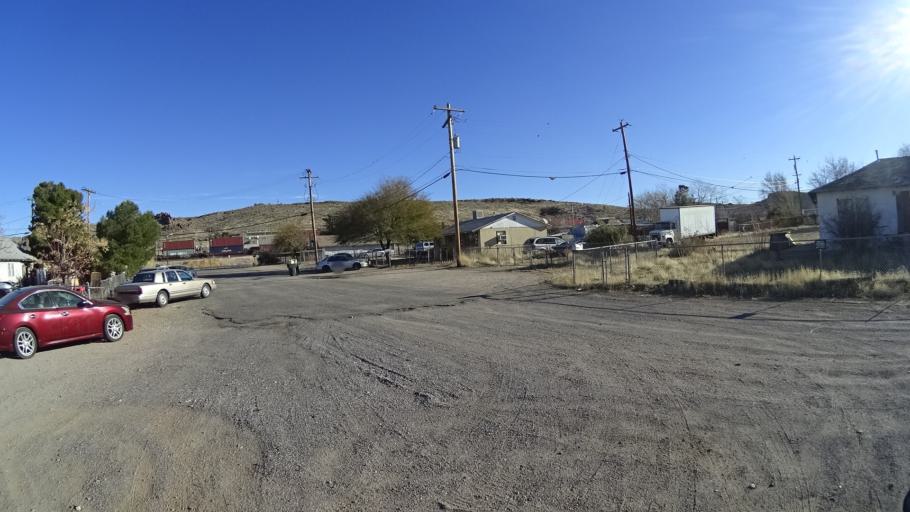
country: US
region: Arizona
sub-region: Mohave County
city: Kingman
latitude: 35.1854
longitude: -114.0459
